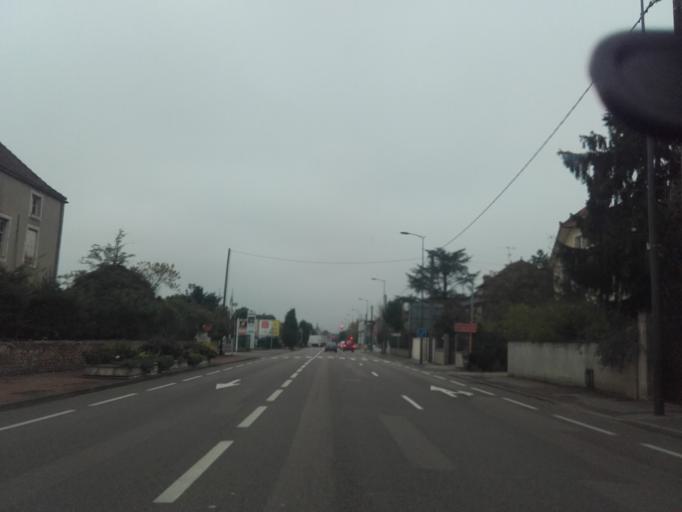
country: FR
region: Bourgogne
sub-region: Departement de la Cote-d'Or
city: Beaune
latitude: 47.0368
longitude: 4.8467
